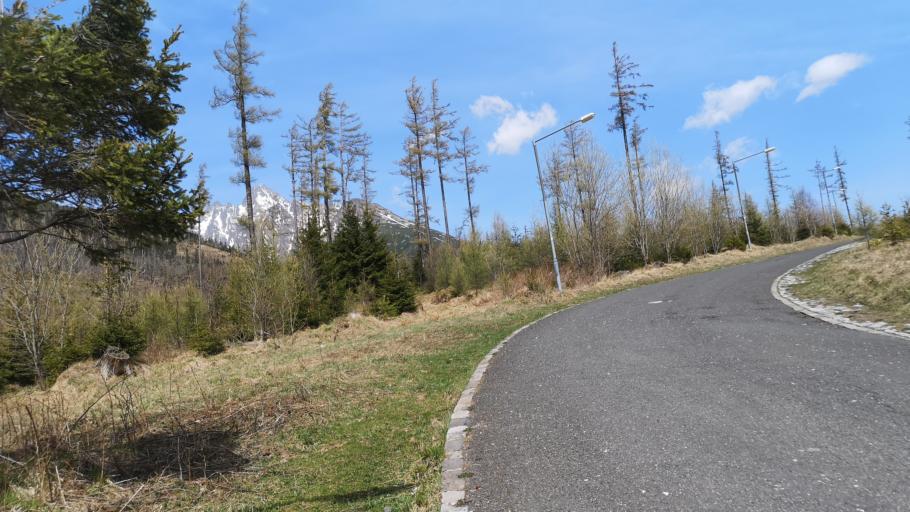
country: SK
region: Presovsky
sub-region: Okres Poprad
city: Vysoke Tatry
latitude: 49.1511
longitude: 20.2247
